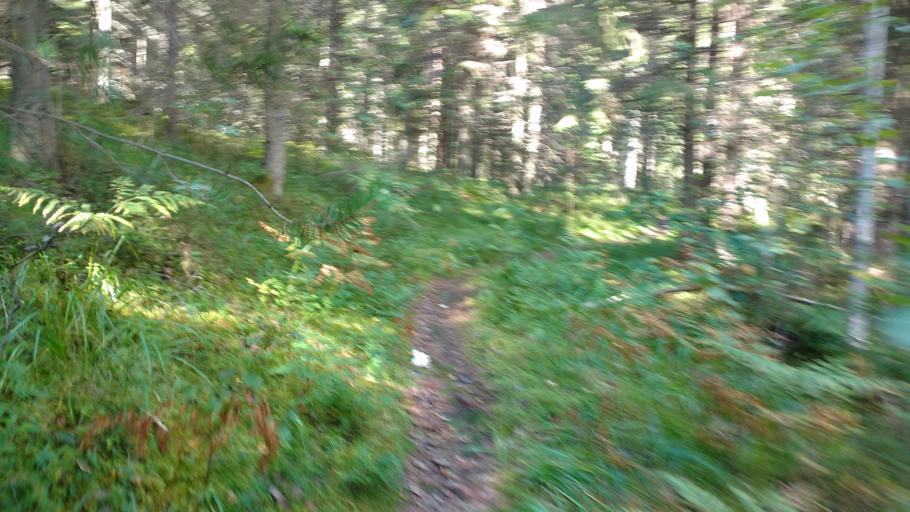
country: FI
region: Varsinais-Suomi
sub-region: Salo
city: Salo
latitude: 60.3539
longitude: 23.1280
